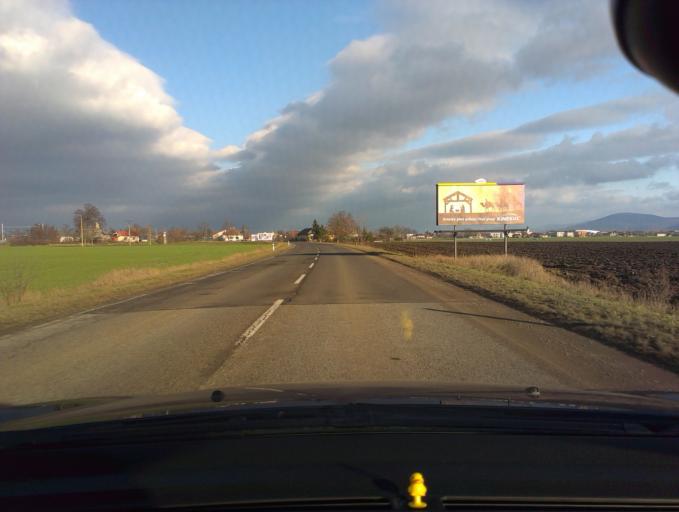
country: SK
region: Nitriansky
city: Cachtice
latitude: 48.6802
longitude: 17.8470
